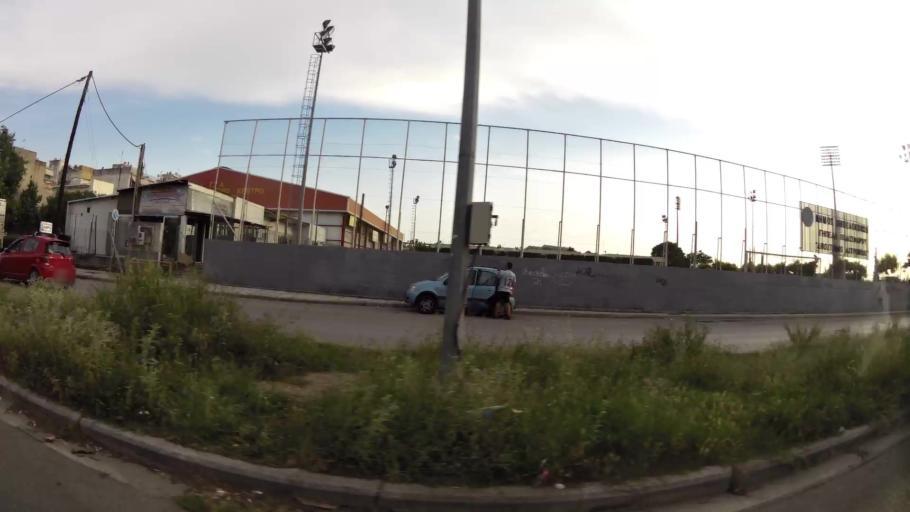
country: GR
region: Central Macedonia
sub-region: Nomos Thessalonikis
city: Ampelokipoi
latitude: 40.6601
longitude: 22.9225
